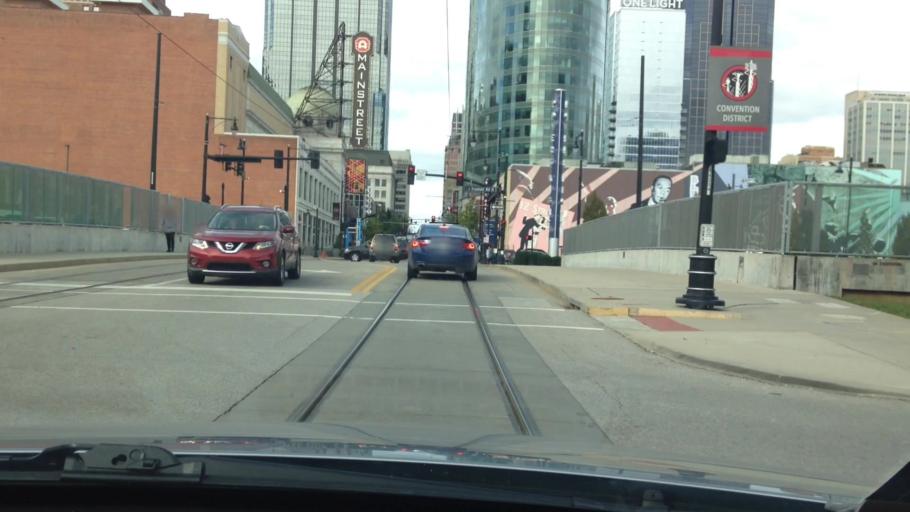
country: US
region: Missouri
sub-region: Jackson County
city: Kansas City
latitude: 39.0957
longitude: -94.5834
